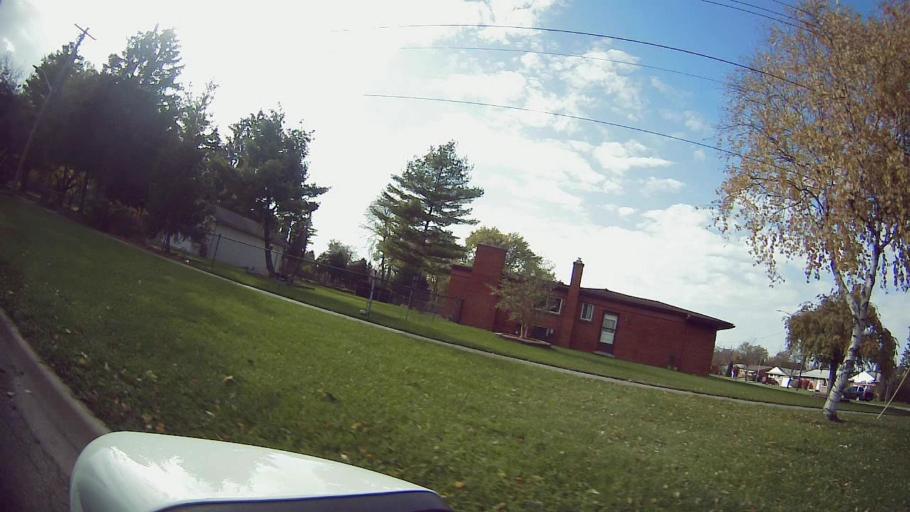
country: US
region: Michigan
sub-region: Oakland County
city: Madison Heights
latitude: 42.4833
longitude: -83.0667
